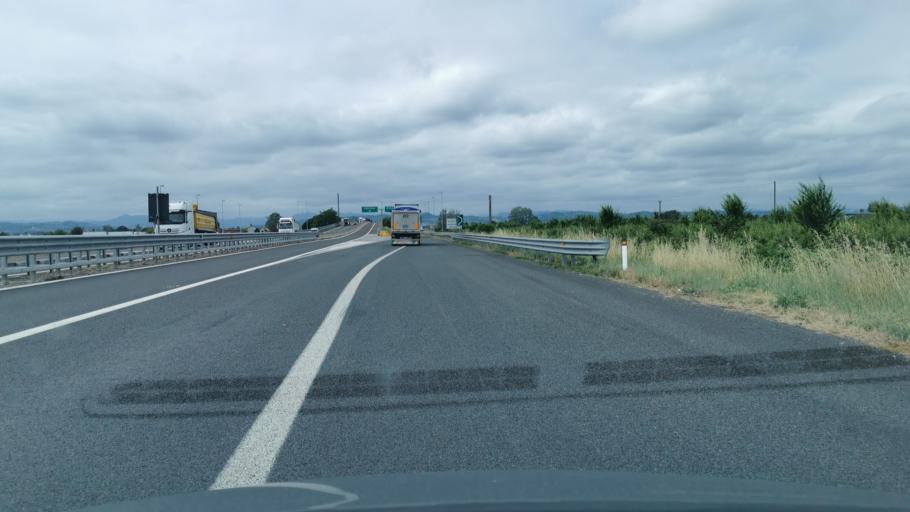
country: IT
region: Emilia-Romagna
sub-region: Provincia di Ravenna
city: Solarolo
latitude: 44.3577
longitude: 11.8200
